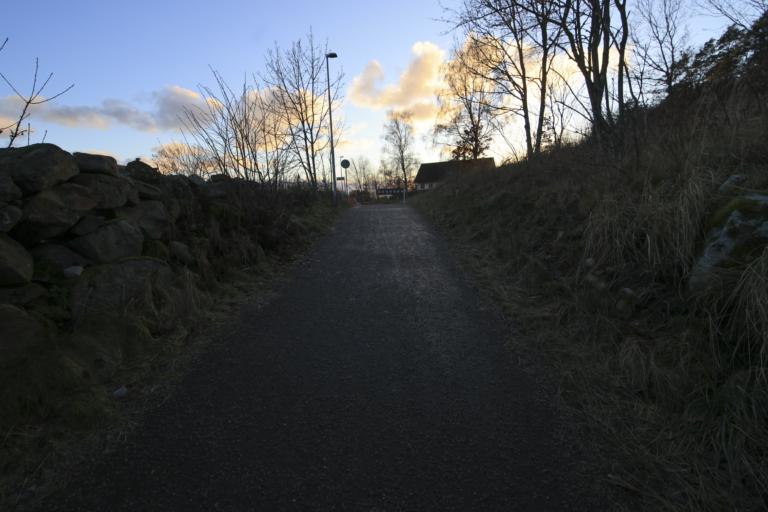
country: SE
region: Halland
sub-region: Varbergs Kommun
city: Varberg
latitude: 57.1381
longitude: 12.2937
